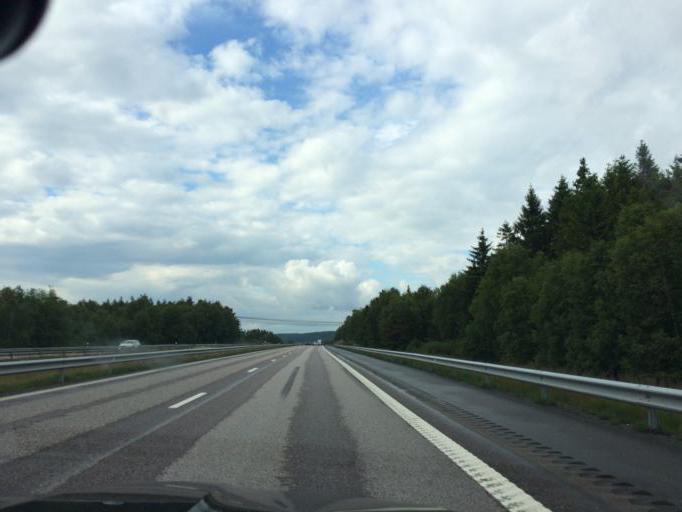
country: SE
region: Halland
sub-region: Kungsbacka Kommun
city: Frillesas
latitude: 57.2790
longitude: 12.2157
